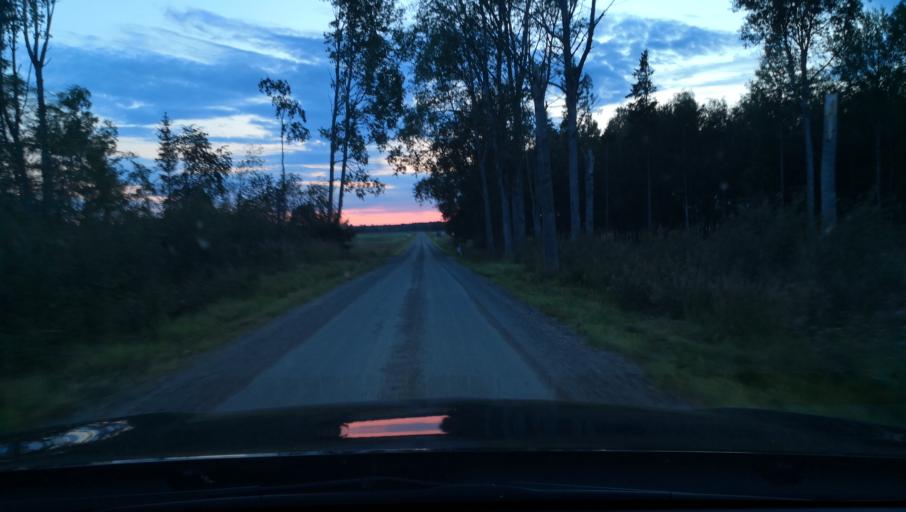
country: SE
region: Uppsala
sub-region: Osthammars Kommun
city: Bjorklinge
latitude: 60.0062
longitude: 17.3346
